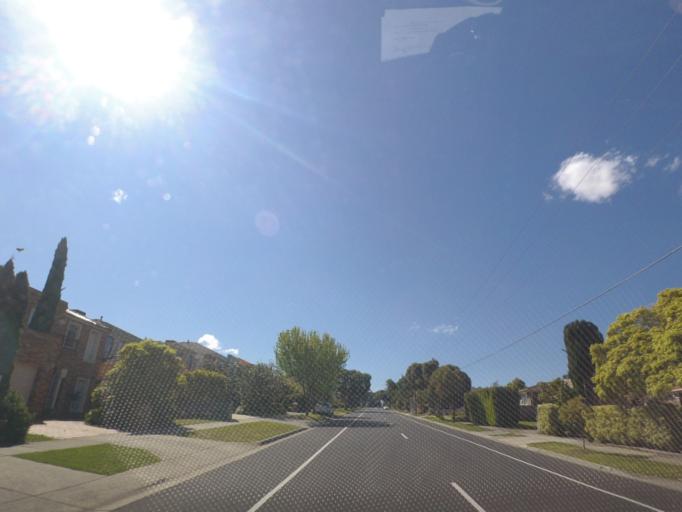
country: AU
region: Victoria
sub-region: Knox
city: Wantirna
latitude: -37.8594
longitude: 145.2276
